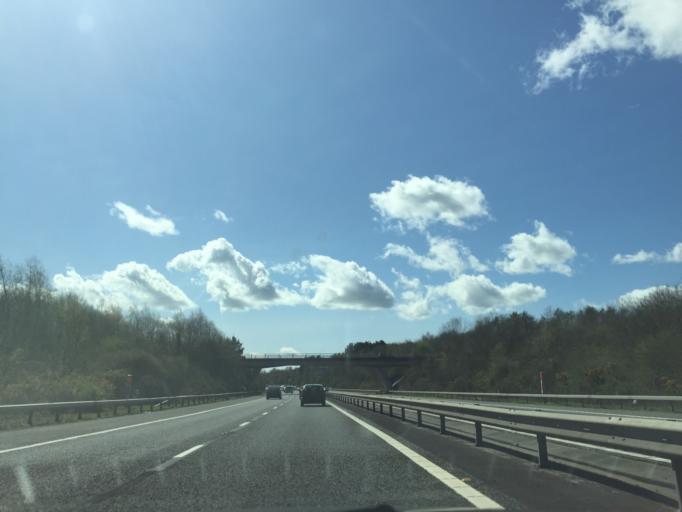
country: GB
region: England
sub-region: Hampshire
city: Waterlooville
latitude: 50.8767
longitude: -1.0126
